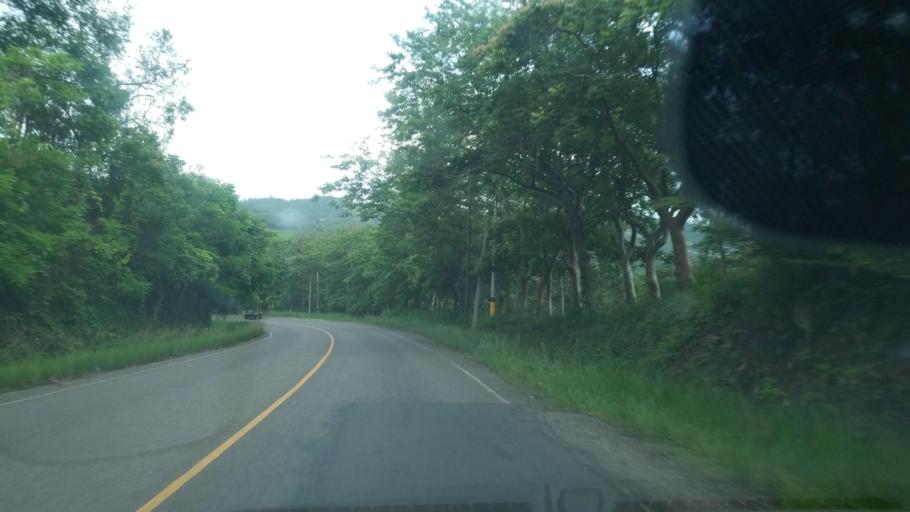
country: HN
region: Santa Barbara
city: Ceguaca
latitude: 14.8108
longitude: -88.1909
